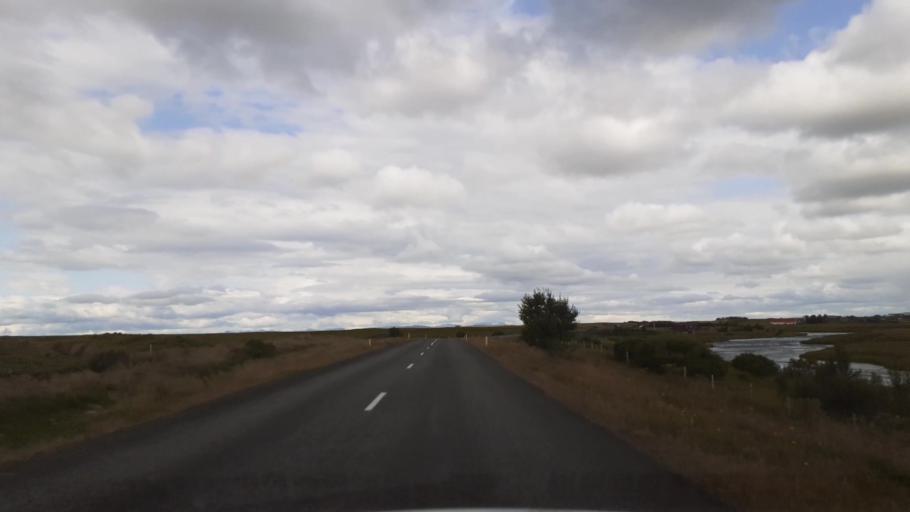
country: IS
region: South
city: Vestmannaeyjar
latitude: 63.8238
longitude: -20.4275
